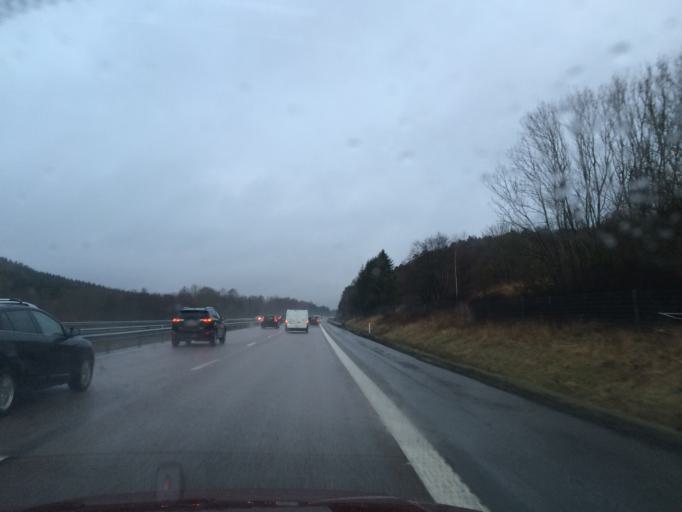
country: SE
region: Halland
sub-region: Kungsbacka Kommun
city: Kungsbacka
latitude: 57.5185
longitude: 12.0505
